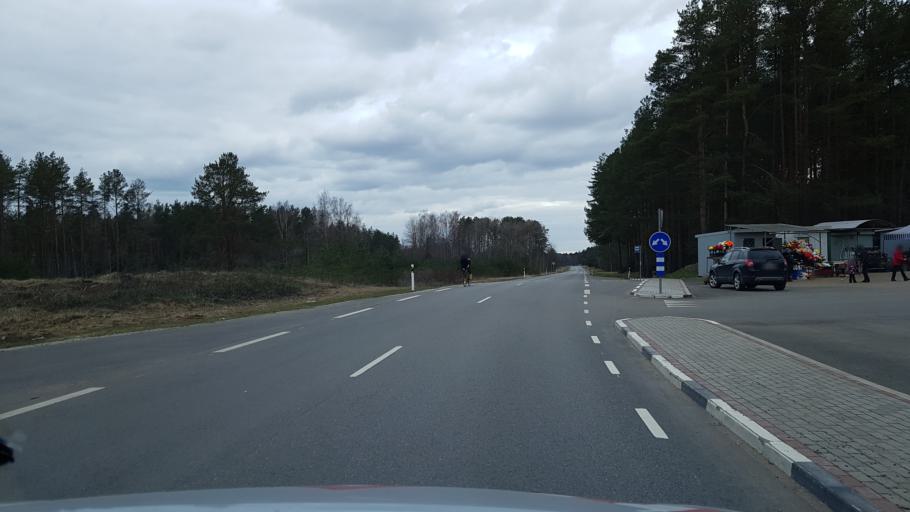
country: EE
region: Ida-Virumaa
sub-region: Narva-Joesuu linn
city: Narva-Joesuu
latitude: 59.4200
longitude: 28.1073
